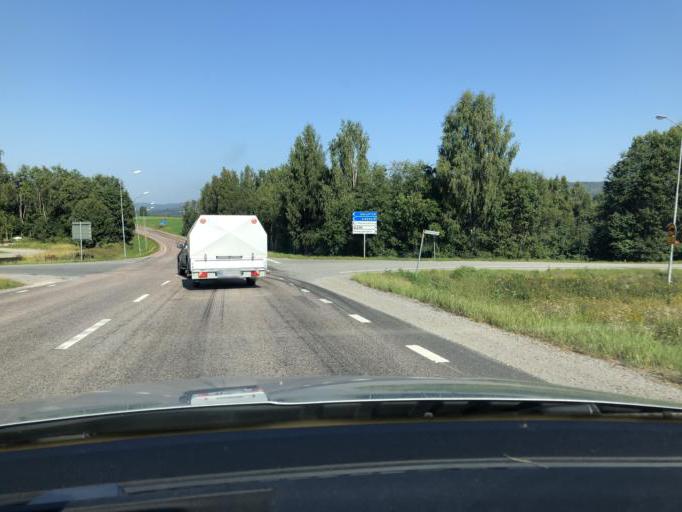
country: SE
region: Vaesternorrland
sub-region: OErnskoeldsviks Kommun
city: Bjasta
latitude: 63.2860
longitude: 18.5669
